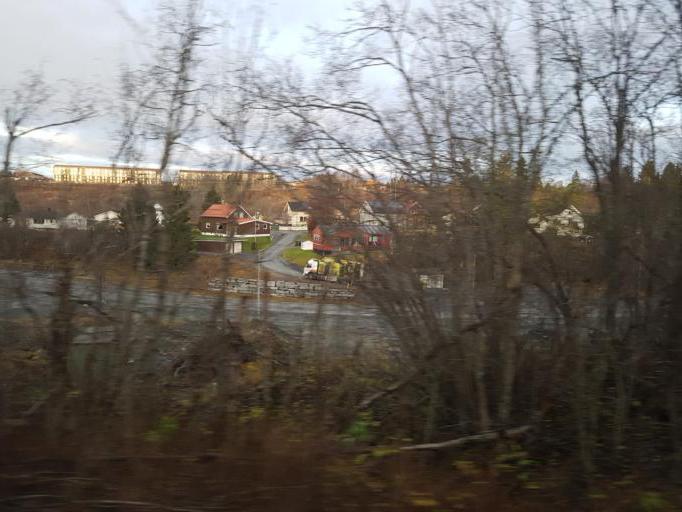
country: NO
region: Sor-Trondelag
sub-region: Melhus
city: Melhus
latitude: 63.3454
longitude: 10.3488
